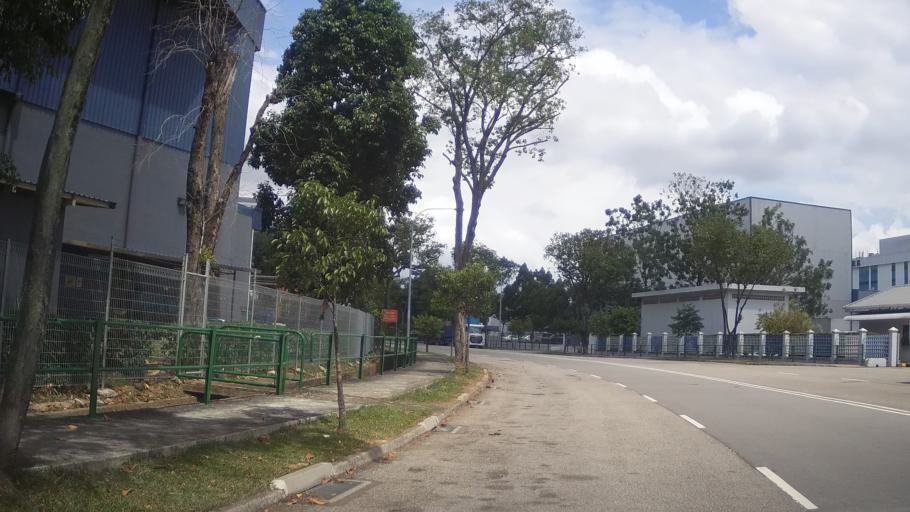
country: MY
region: Johor
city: Johor Bahru
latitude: 1.3238
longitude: 103.6674
